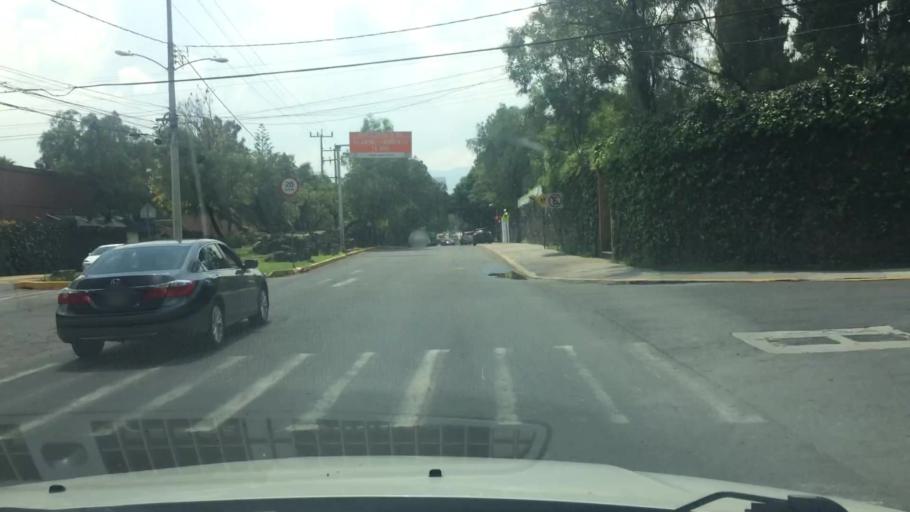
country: MX
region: Mexico City
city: Magdalena Contreras
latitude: 19.3169
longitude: -99.2023
